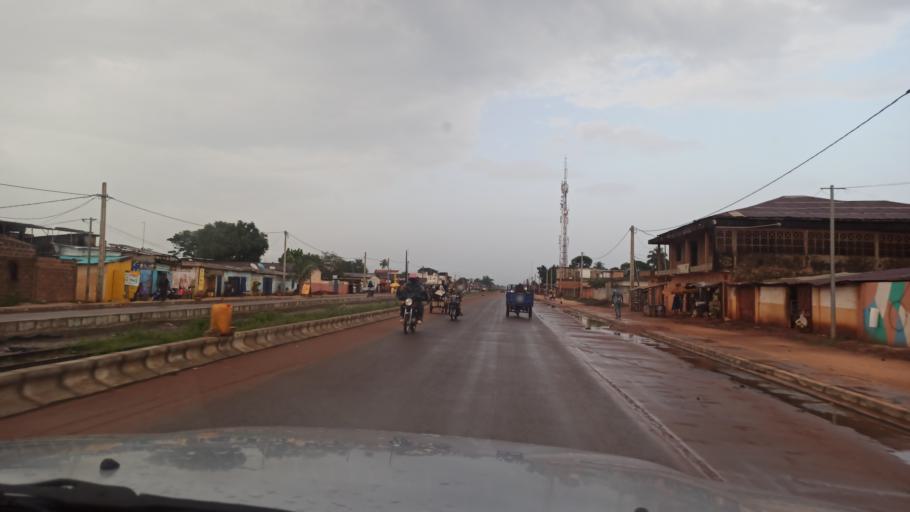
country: BJ
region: Queme
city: Porto-Novo
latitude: 6.4931
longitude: 2.6261
